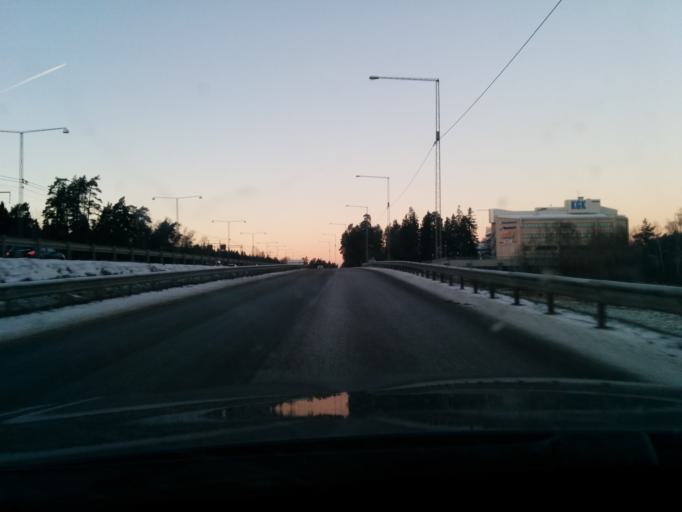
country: SE
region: Stockholm
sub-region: Sollentuna Kommun
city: Sollentuna
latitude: 59.4405
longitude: 17.9243
